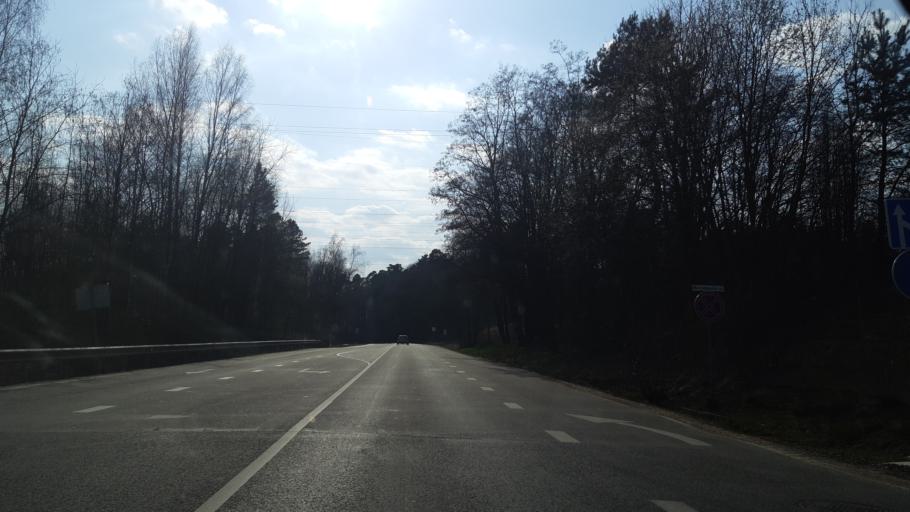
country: LT
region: Kauno apskritis
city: Dainava (Kaunas)
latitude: 54.8715
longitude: 23.9922
